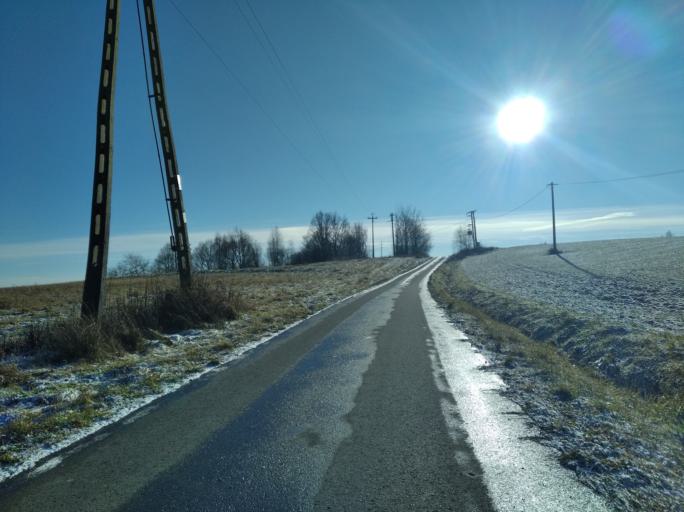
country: PL
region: Subcarpathian Voivodeship
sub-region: Powiat strzyzowski
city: Czudec
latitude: 49.9438
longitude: 21.7668
